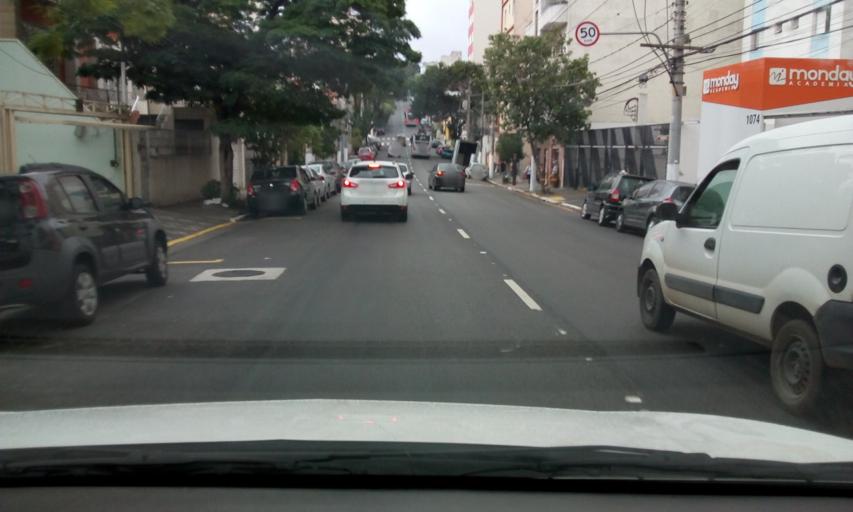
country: BR
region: Sao Paulo
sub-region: Sao Paulo
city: Sao Paulo
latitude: -23.5719
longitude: -46.6243
